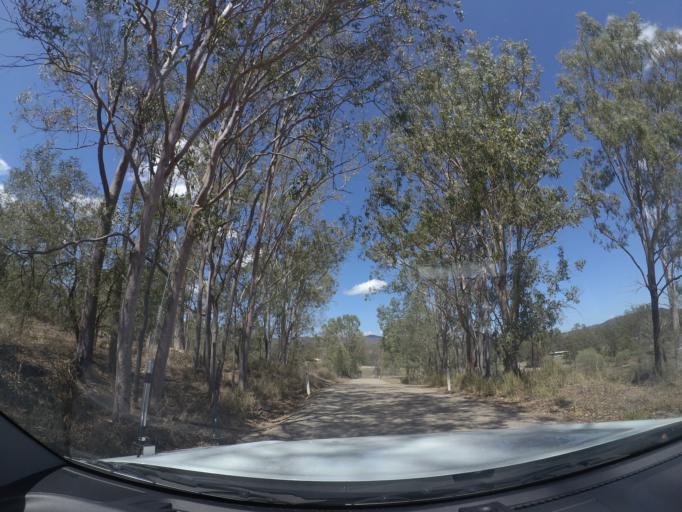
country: AU
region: Queensland
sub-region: Logan
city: Cedar Vale
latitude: -27.8486
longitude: 152.8958
